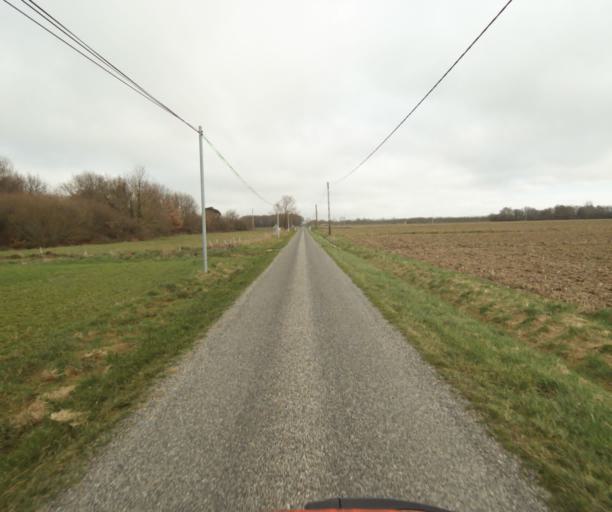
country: FR
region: Midi-Pyrenees
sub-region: Departement de l'Ariege
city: Mazeres
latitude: 43.1826
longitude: 1.6799
